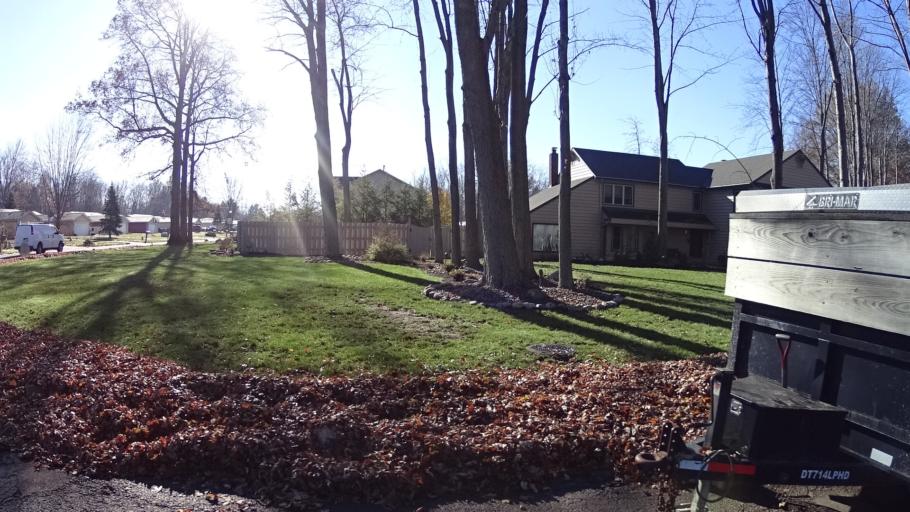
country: US
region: Ohio
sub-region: Lorain County
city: North Ridgeville
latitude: 41.4089
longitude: -81.9951
